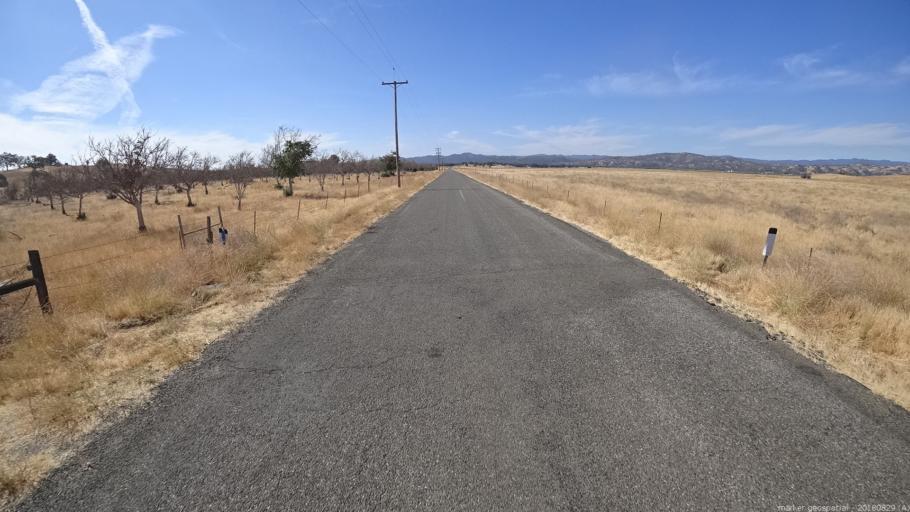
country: US
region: California
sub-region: Monterey County
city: King City
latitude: 35.9551
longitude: -121.1176
